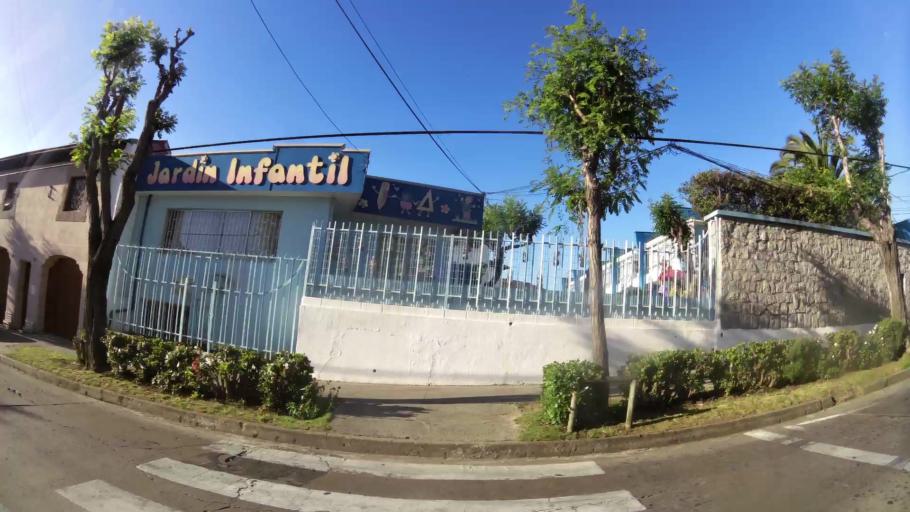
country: CL
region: Valparaiso
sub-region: Provincia de Valparaiso
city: Vina del Mar
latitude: -33.0267
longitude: -71.5729
